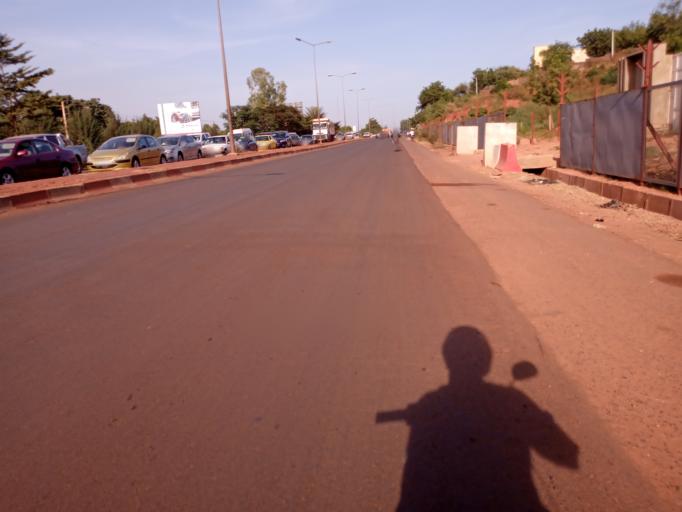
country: ML
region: Bamako
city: Bamako
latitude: 12.6147
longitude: -7.9909
